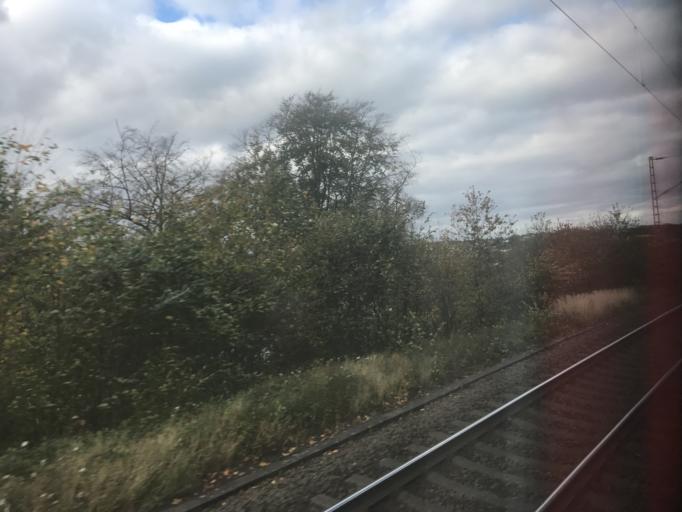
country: DE
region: North Rhine-Westphalia
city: Gevelsberg
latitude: 51.3123
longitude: 7.3420
